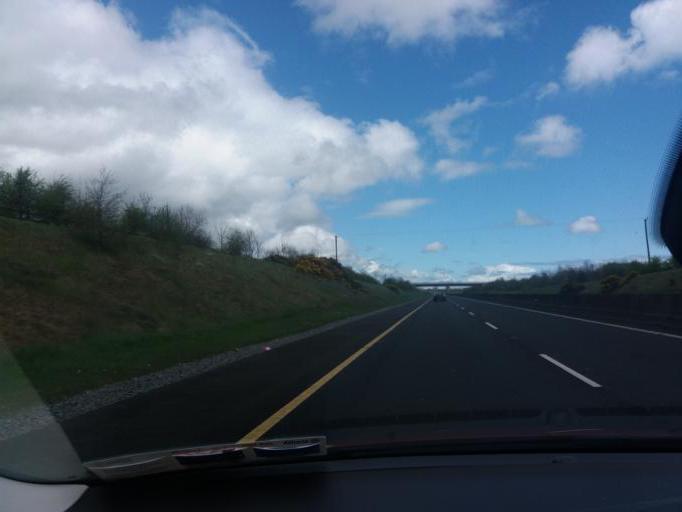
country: IE
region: Munster
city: Thurles
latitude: 52.6534
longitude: -7.7439
